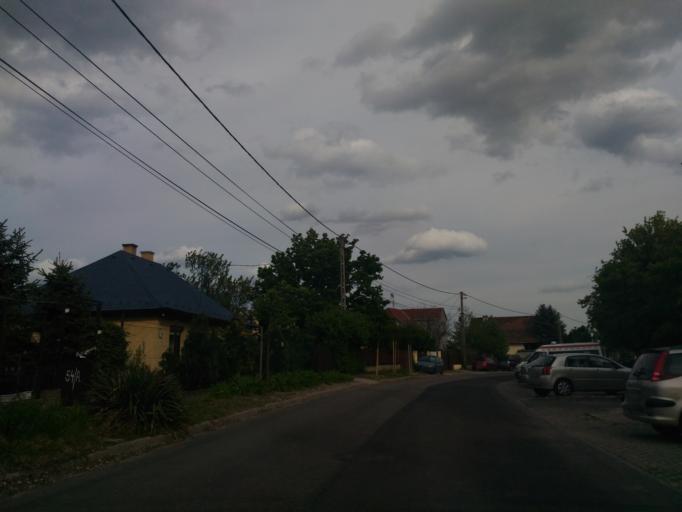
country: HU
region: Budapest
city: Budapest XXII. keruelet
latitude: 47.4297
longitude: 19.0217
